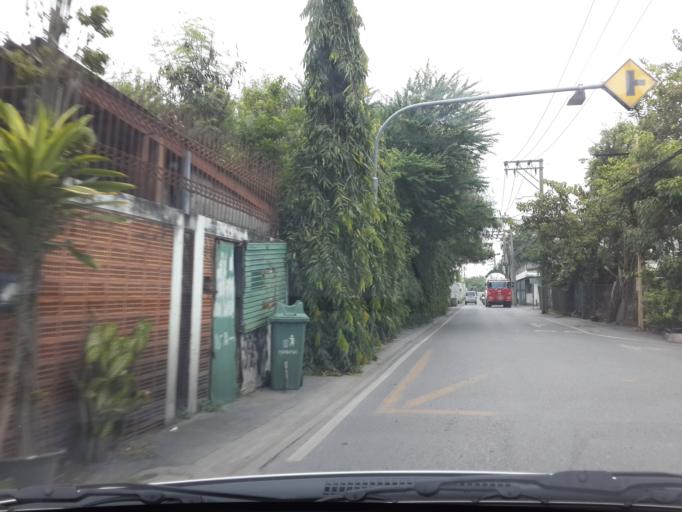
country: TH
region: Bangkok
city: Huai Khwang
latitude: 13.7613
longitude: 100.5917
